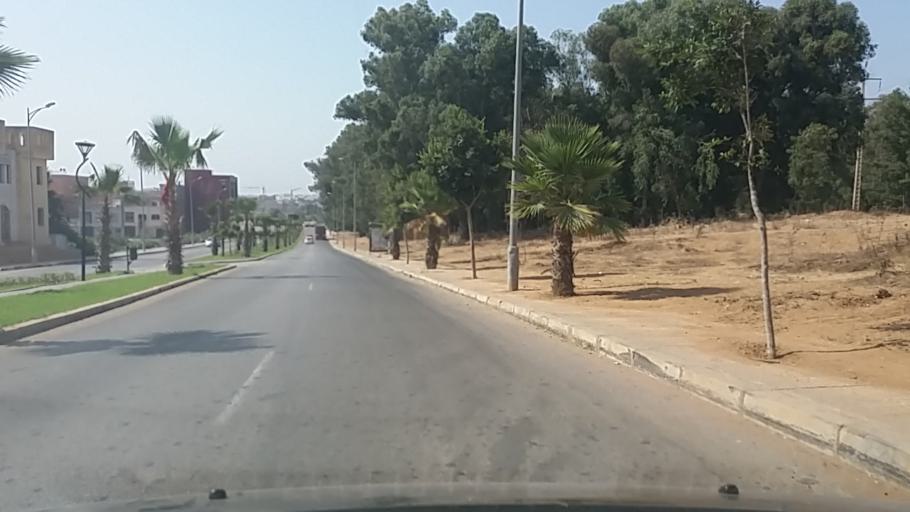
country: MA
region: Gharb-Chrarda-Beni Hssen
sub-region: Kenitra Province
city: Kenitra
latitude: 34.2512
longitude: -6.6151
